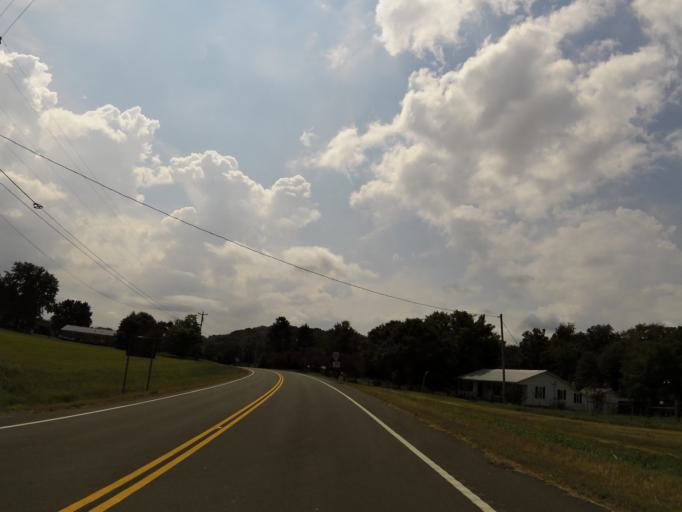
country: US
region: Tennessee
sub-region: Perry County
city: Linden
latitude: 35.7375
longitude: -87.8106
